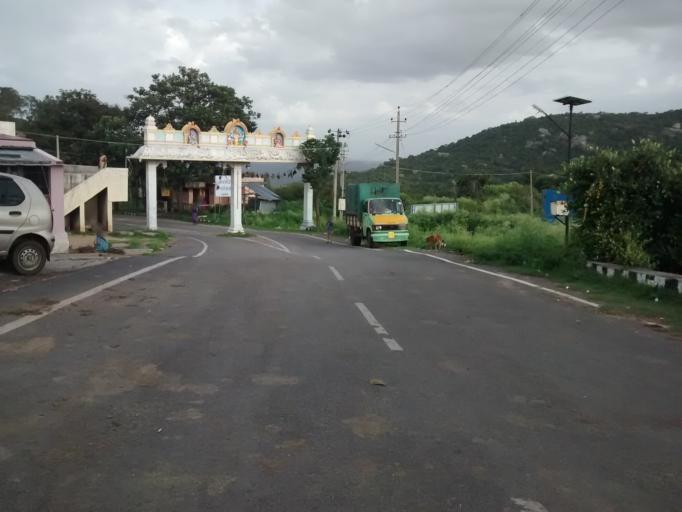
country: IN
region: Karnataka
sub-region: Tumkur
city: Tumkur
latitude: 13.3723
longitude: 77.2078
